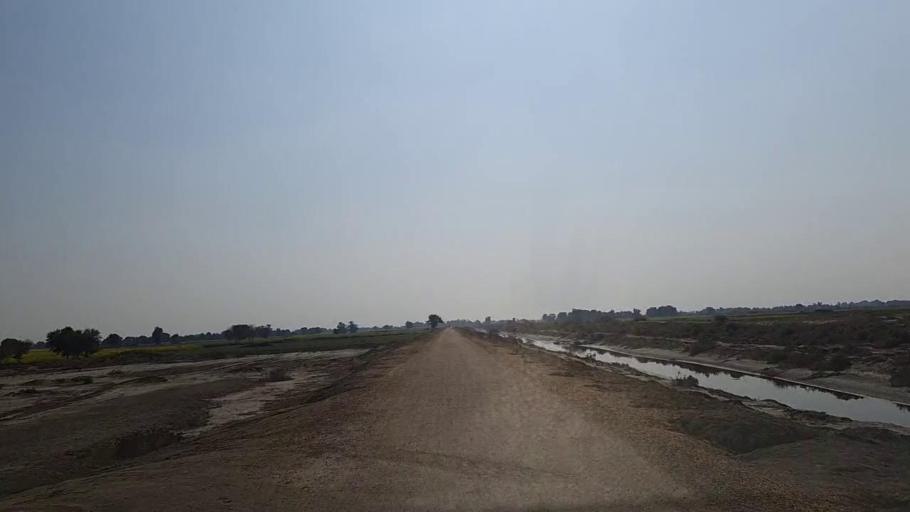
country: PK
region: Sindh
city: Nawabshah
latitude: 26.2620
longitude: 68.5031
